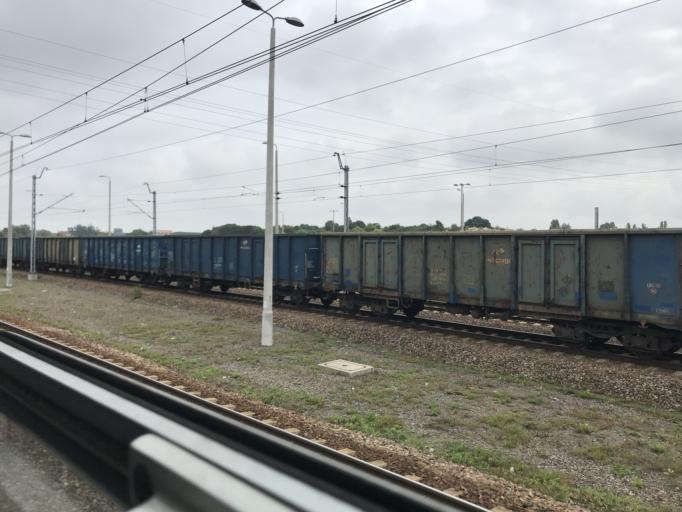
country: PL
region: Pomeranian Voivodeship
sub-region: Gdansk
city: Gdansk
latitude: 54.3342
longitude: 18.6391
